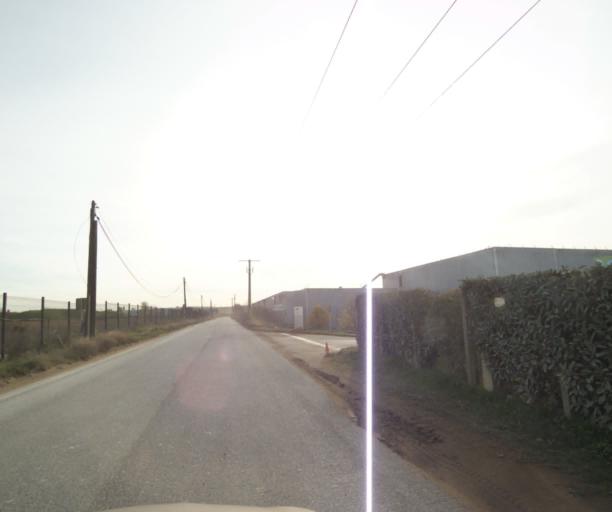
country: FR
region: Ile-de-France
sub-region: Departement des Yvelines
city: Medan
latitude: 48.9510
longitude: 2.0113
